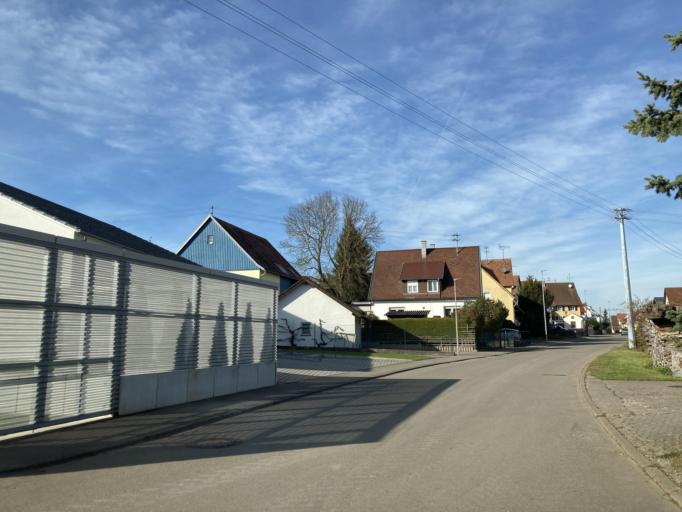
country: DE
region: Baden-Wuerttemberg
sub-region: Tuebingen Region
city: Hirrlingen
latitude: 48.4147
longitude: 8.9193
